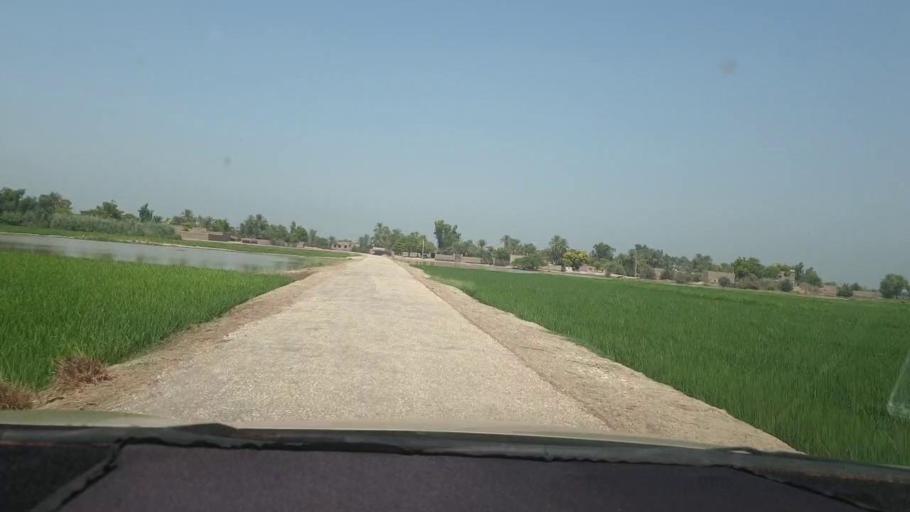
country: PK
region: Sindh
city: Kambar
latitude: 27.6224
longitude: 68.0527
